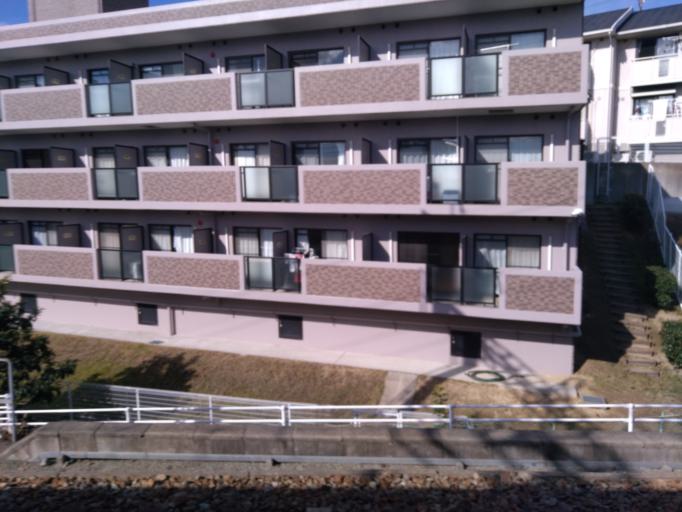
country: JP
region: Hyogo
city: Takarazuka
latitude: 34.8108
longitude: 135.3452
